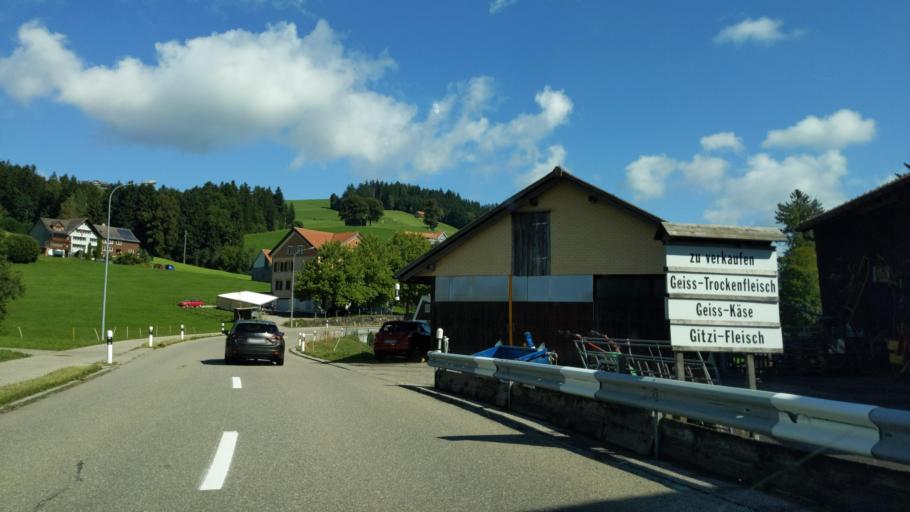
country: CH
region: Saint Gallen
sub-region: Wahlkreis Toggenburg
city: Sankt Peterzell
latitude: 47.3232
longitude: 9.2075
